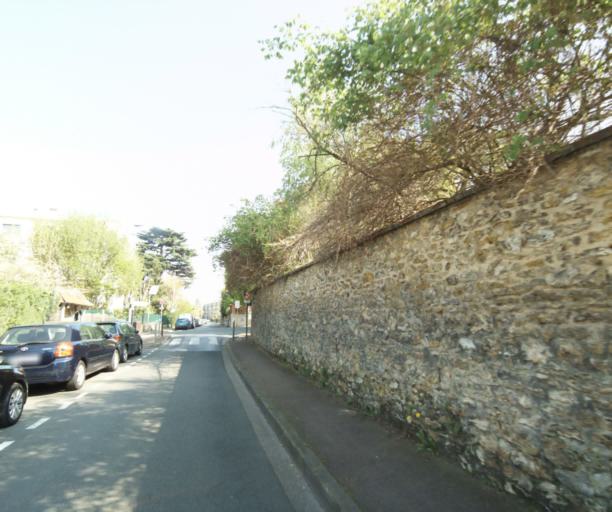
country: FR
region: Ile-de-France
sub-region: Departement des Hauts-de-Seine
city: Sevres
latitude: 48.8229
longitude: 2.2168
